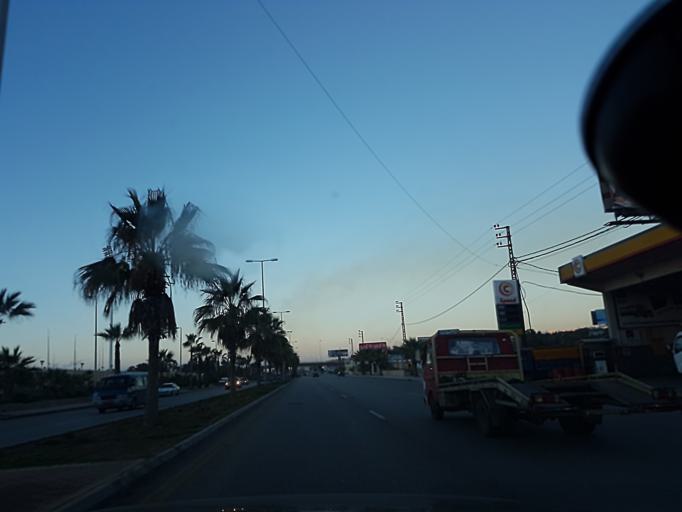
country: LB
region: Liban-Sud
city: Sidon
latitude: 33.5842
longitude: 35.3858
